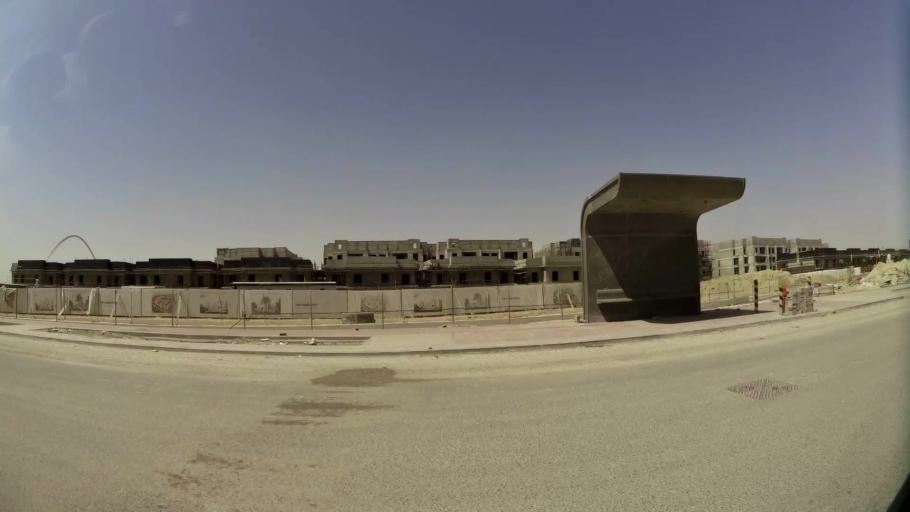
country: QA
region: Baladiyat Umm Salal
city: Umm Salal Muhammad
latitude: 25.4049
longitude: 51.5176
